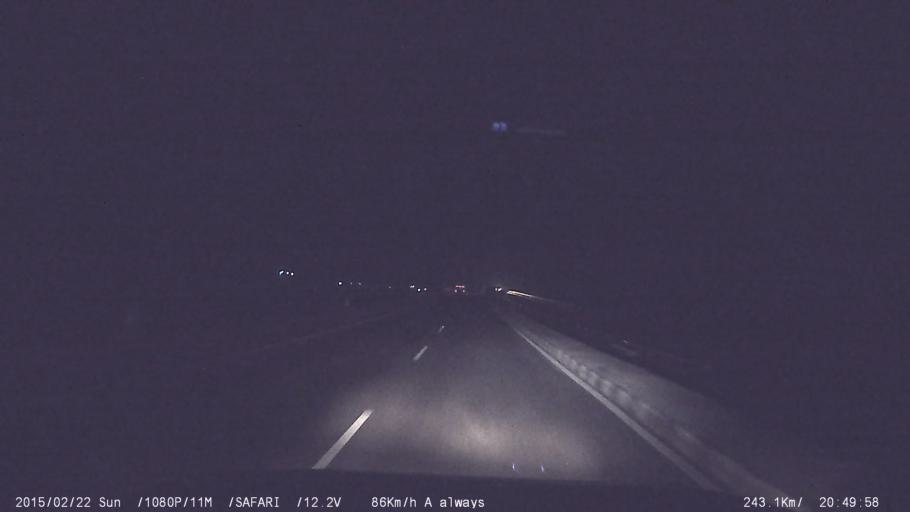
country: IN
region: Tamil Nadu
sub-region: Dindigul
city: Vedasandur
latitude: 10.5250
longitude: 77.9355
